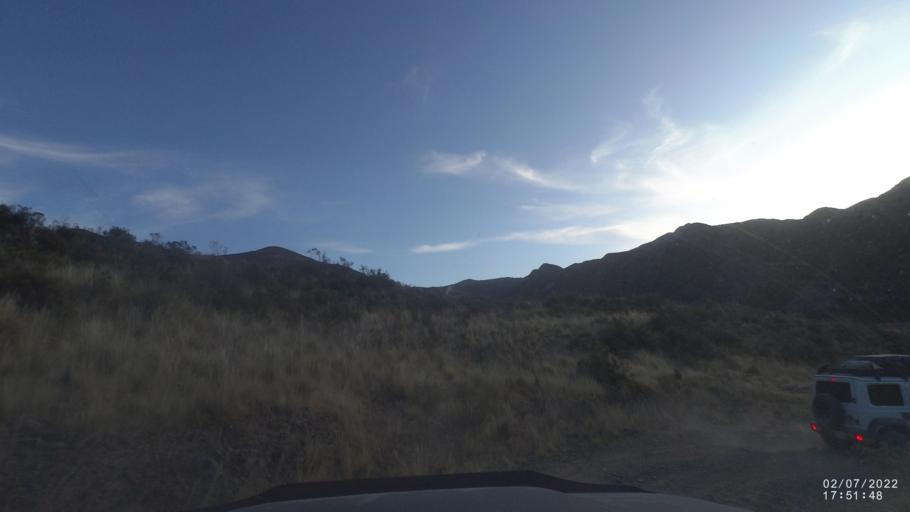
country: BO
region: Cochabamba
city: Irpa Irpa
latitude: -17.8476
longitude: -66.6182
